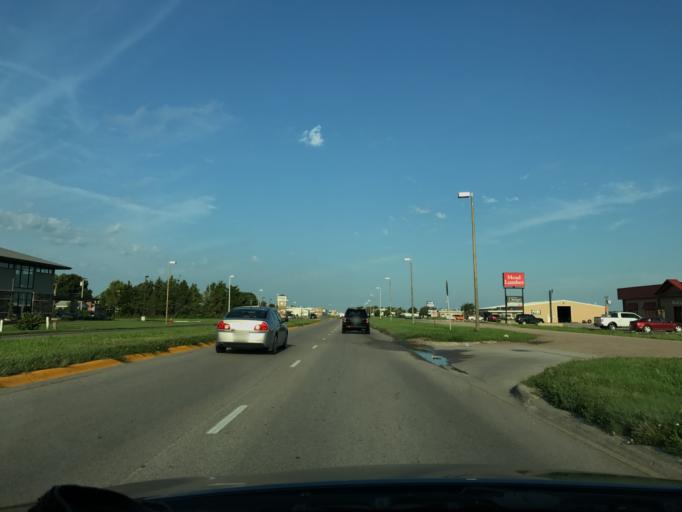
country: US
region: Nebraska
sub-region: Platte County
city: Columbus
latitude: 41.4386
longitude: -97.3327
